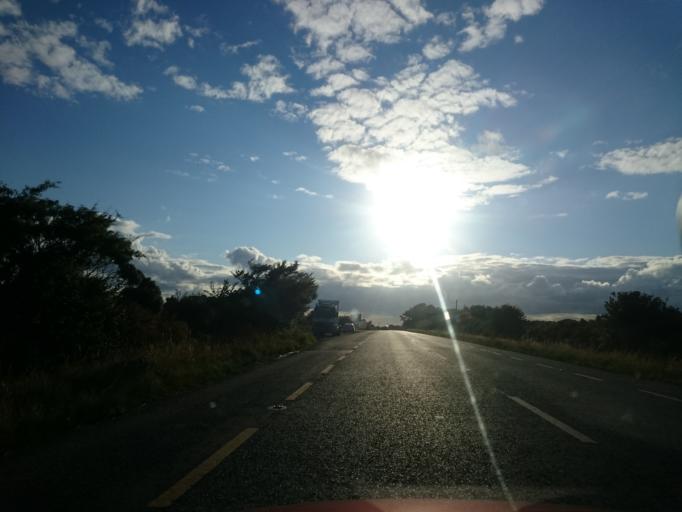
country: IE
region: Leinster
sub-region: Loch Garman
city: Ballygerry
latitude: 52.2442
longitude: -6.3650
